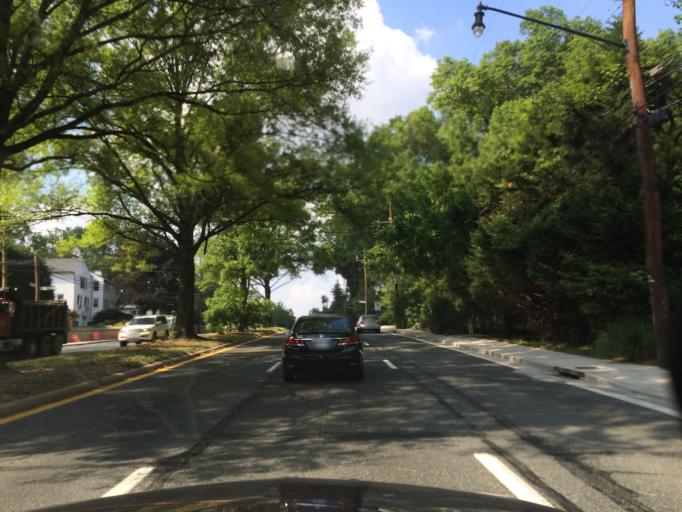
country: US
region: Maryland
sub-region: Montgomery County
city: South Kensington
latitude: 39.0188
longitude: -77.0777
